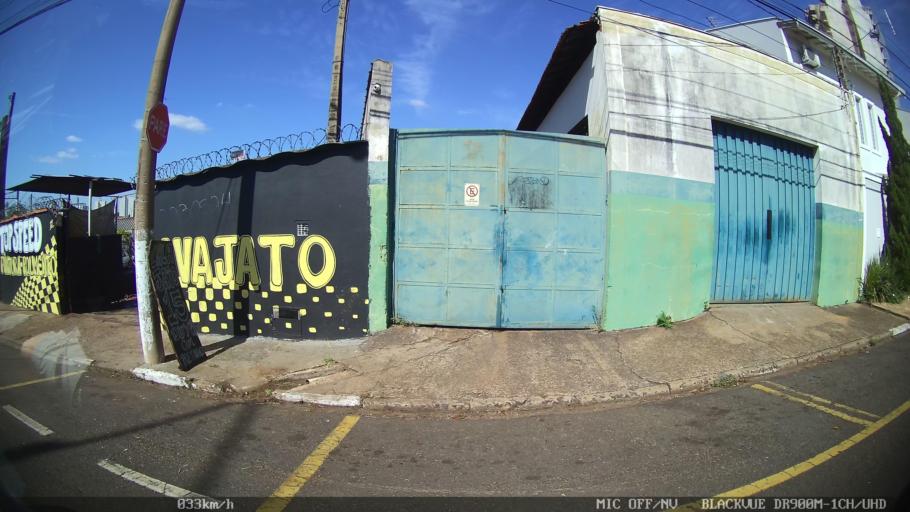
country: BR
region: Sao Paulo
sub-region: Franca
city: Franca
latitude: -20.5359
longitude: -47.4101
